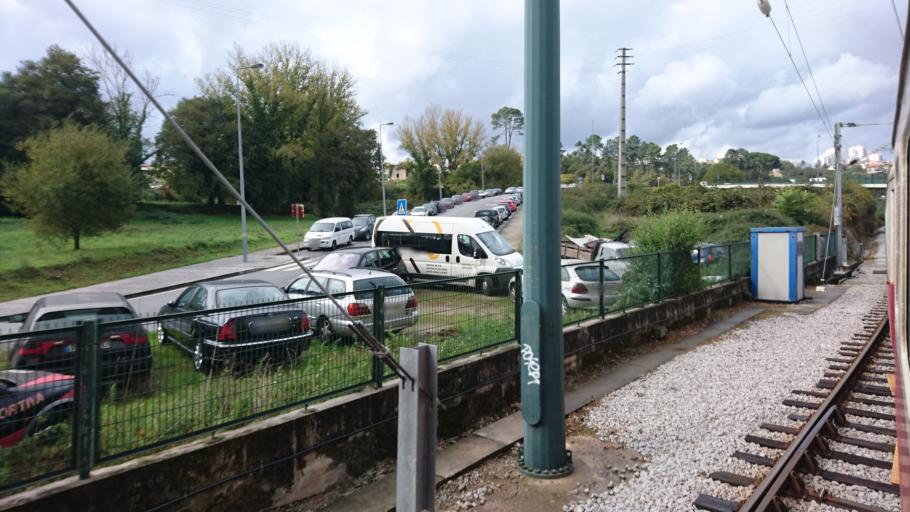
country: PT
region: Porto
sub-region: Marco de Canaveses
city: Marco de Canavezes
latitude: 41.1823
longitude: -8.1380
